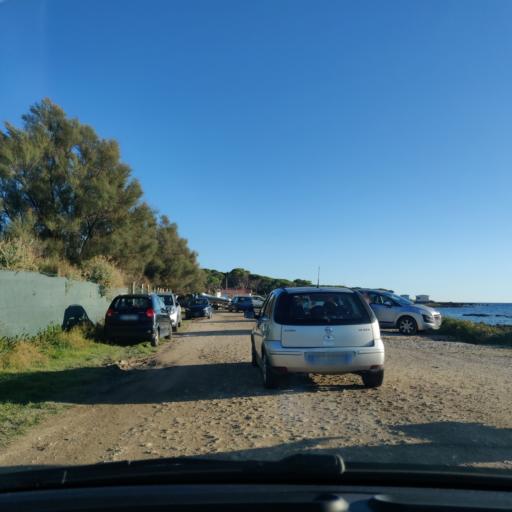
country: IT
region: Latium
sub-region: Citta metropolitana di Roma Capitale
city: Aurelia
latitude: 42.1488
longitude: 11.7440
